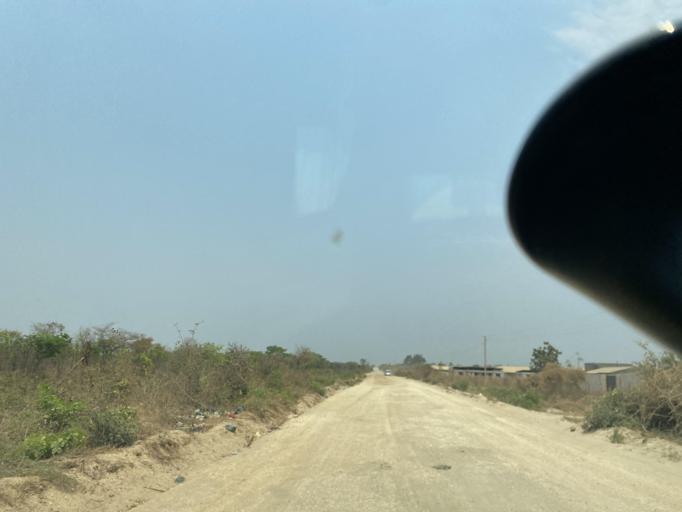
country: ZM
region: Lusaka
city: Lusaka
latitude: -15.5202
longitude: 28.3421
